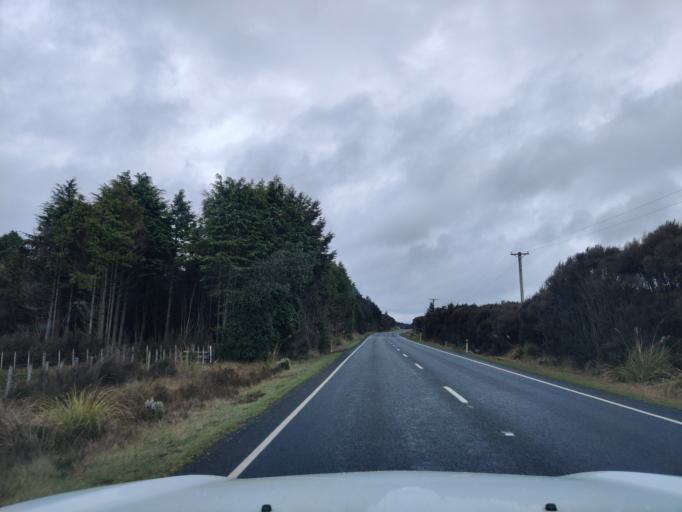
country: NZ
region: Manawatu-Wanganui
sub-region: Ruapehu District
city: Waiouru
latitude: -39.3361
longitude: 175.3796
